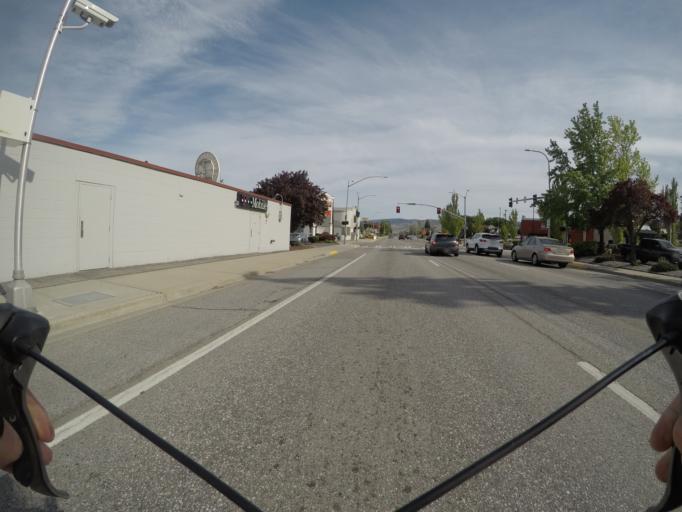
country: US
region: Washington
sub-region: Chelan County
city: Wenatchee
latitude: 47.4302
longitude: -120.3192
